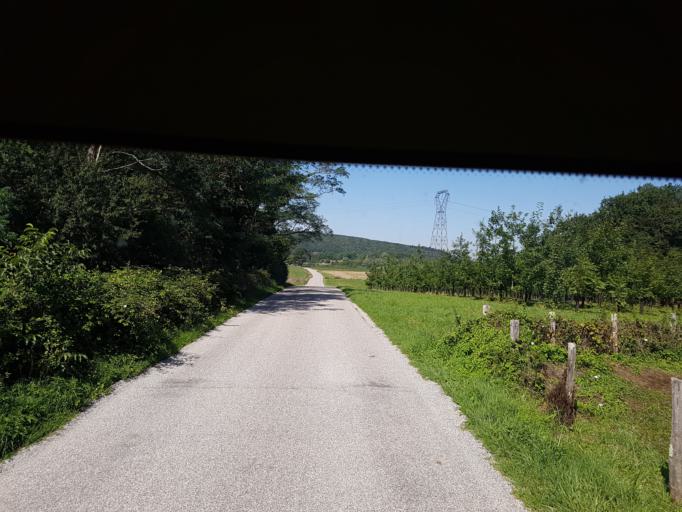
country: FR
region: Franche-Comte
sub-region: Departement du Jura
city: Perrigny
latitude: 46.7331
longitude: 5.5700
